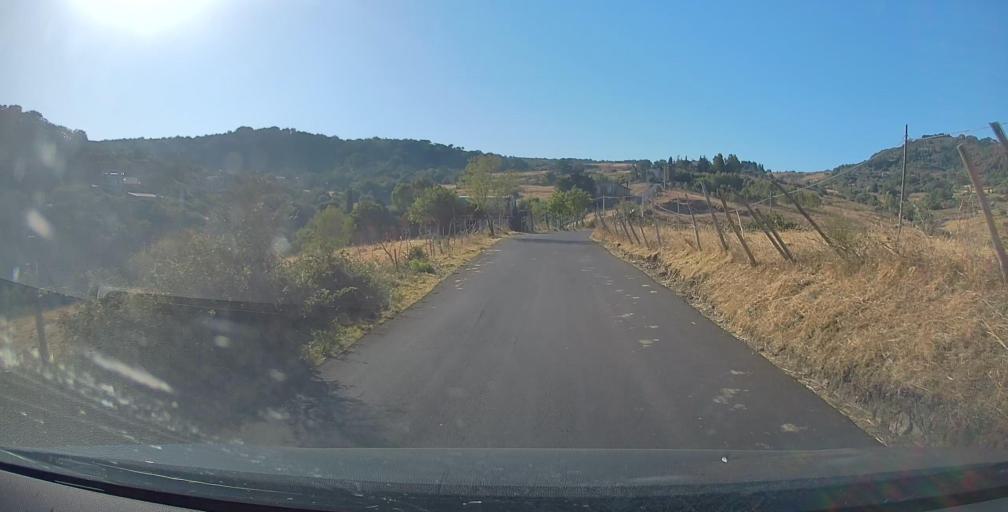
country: IT
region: Sicily
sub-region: Messina
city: San Piero Patti
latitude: 38.0614
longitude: 14.9906
